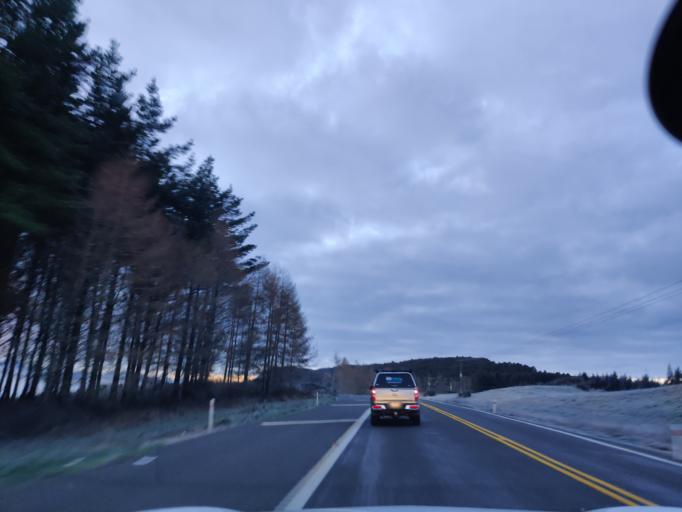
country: NZ
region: Waikato
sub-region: South Waikato District
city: Tokoroa
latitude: -38.3998
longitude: 176.0474
